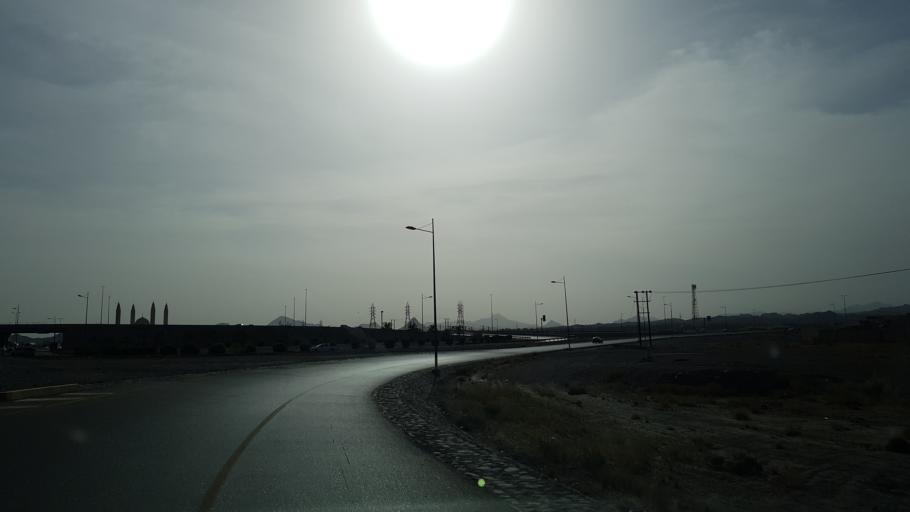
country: OM
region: Muhafazat ad Dakhiliyah
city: Nizwa
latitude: 22.8605
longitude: 57.5423
